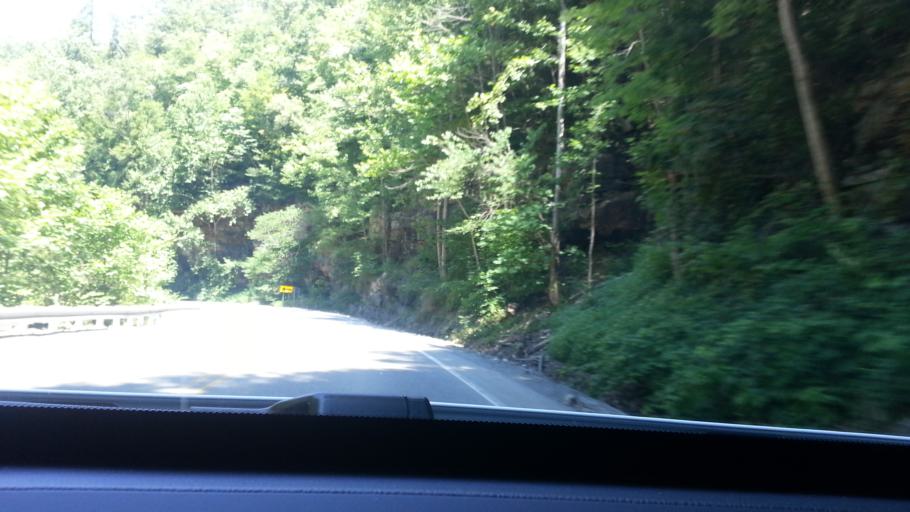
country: US
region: West Virginia
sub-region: Fayette County
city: Ansted
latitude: 38.1054
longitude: -81.1482
